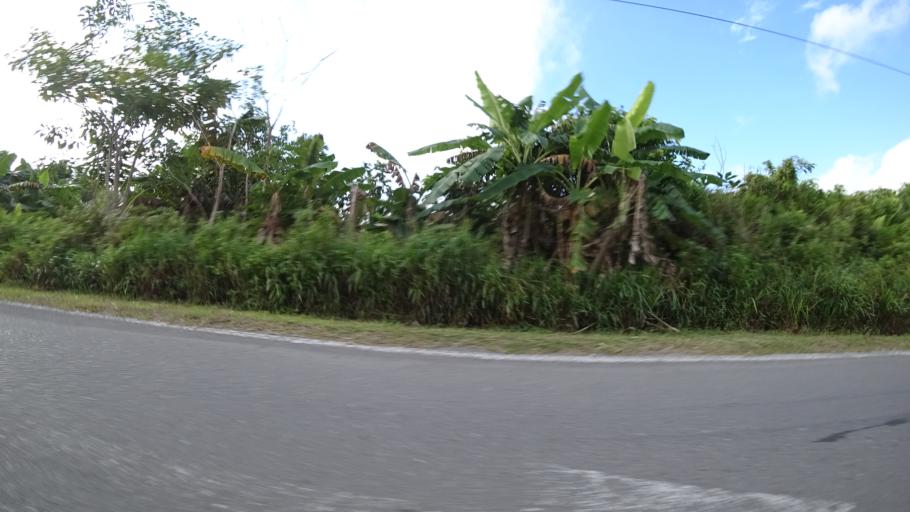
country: MY
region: Sarawak
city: Miri
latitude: 4.5514
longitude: 114.0158
